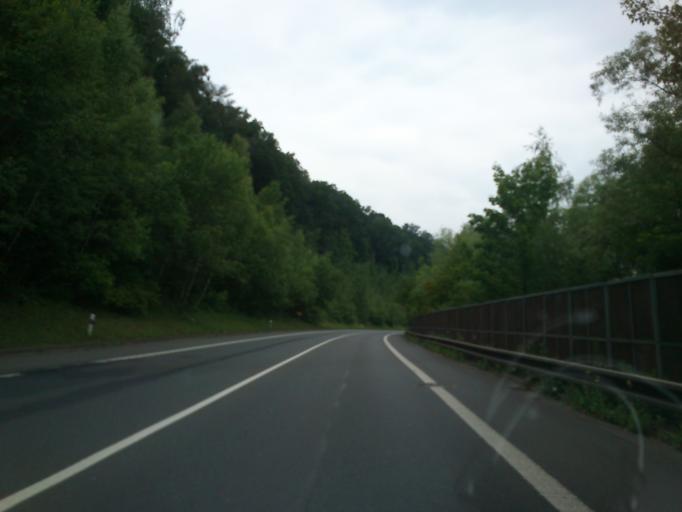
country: CZ
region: Central Bohemia
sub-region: Okres Mlada Boleslav
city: Mlada Boleslav
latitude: 50.4468
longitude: 14.8772
